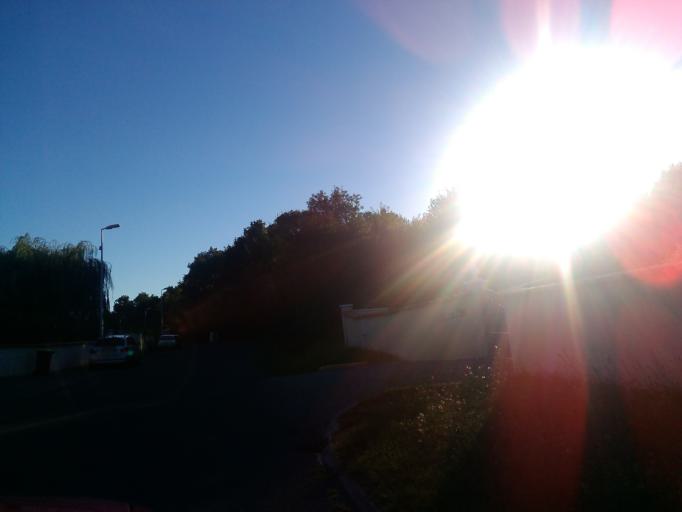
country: FR
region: Poitou-Charentes
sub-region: Departement de la Charente-Maritime
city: Chaillevette
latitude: 45.7210
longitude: -1.0704
